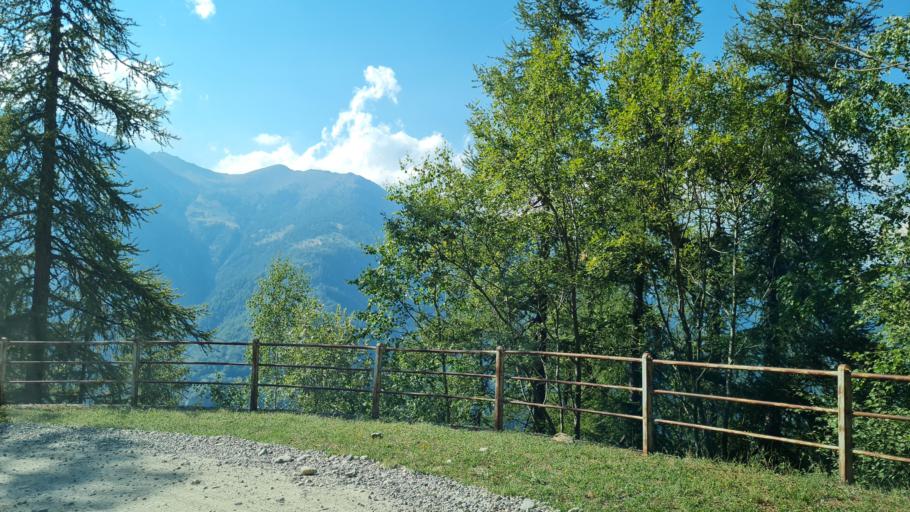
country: IT
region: Aosta Valley
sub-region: Valle d'Aosta
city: Fontainemore
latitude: 45.6328
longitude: 7.8660
